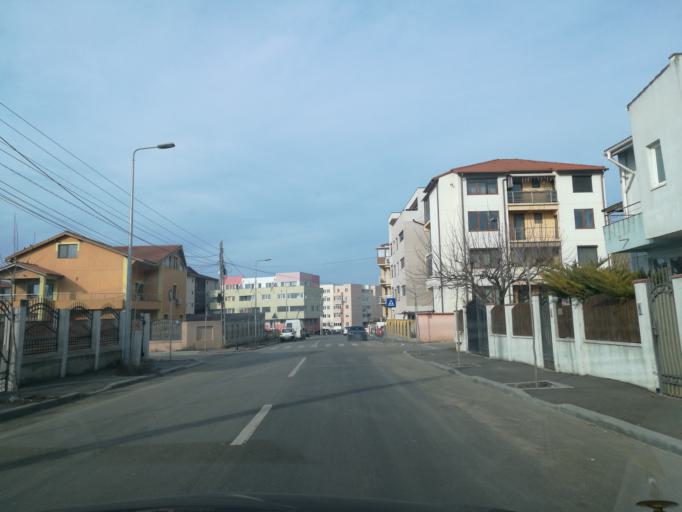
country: RO
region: Constanta
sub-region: Municipiul Constanta
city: Constanta
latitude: 44.1842
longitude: 28.6113
